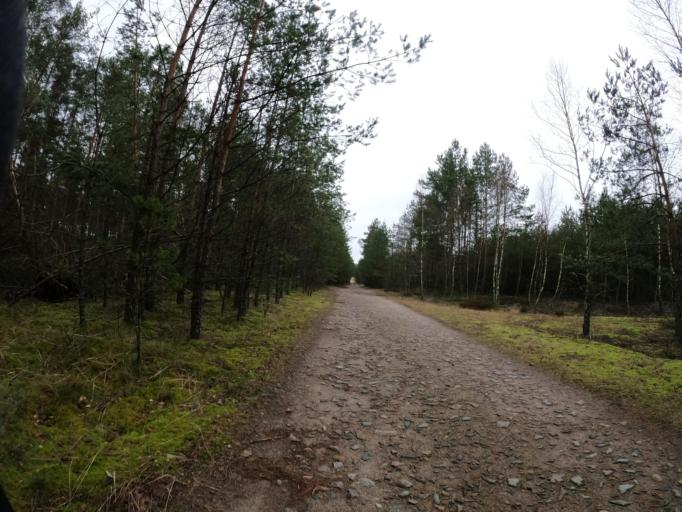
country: PL
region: Greater Poland Voivodeship
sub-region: Powiat zlotowski
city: Sypniewo
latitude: 53.5039
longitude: 16.5611
